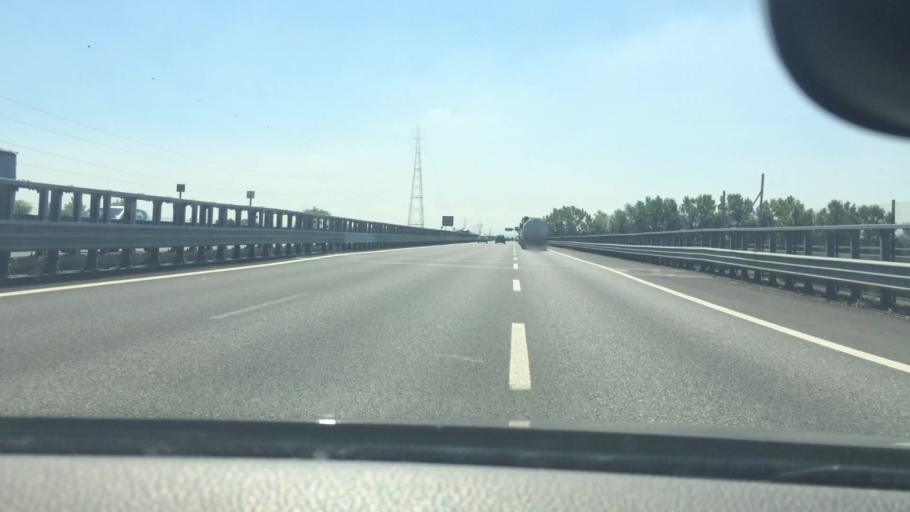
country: IT
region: Emilia-Romagna
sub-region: Provincia di Piacenza
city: Piacenza
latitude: 45.0662
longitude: 9.7337
